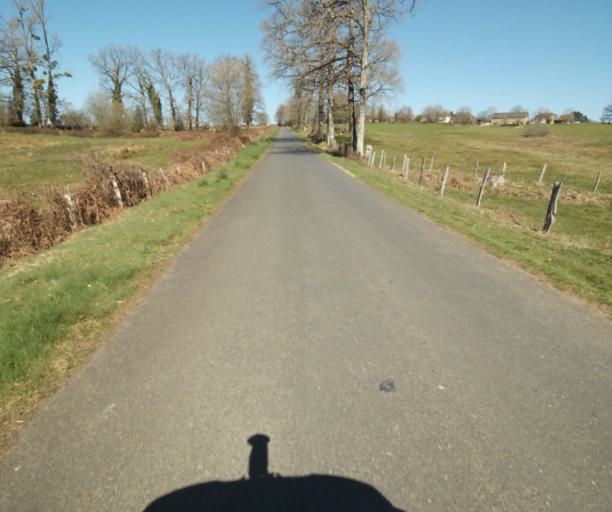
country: FR
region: Limousin
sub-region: Departement de la Correze
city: Saint-Clement
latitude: 45.3325
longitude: 1.6564
